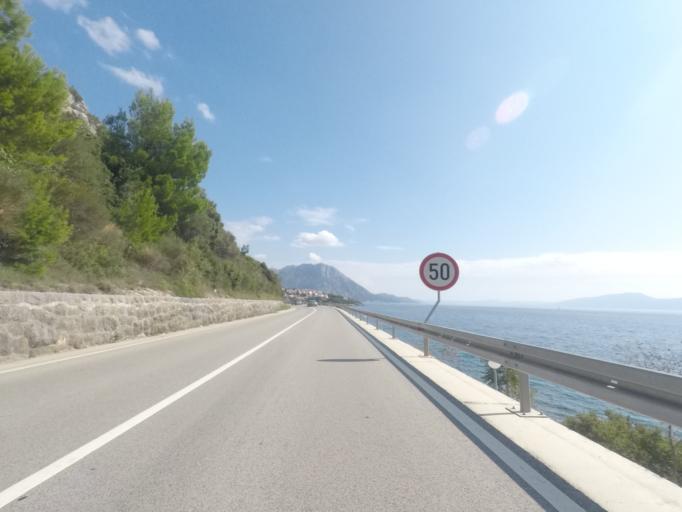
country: HR
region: Splitsko-Dalmatinska
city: Vrgorac
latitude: 43.1277
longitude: 17.2906
